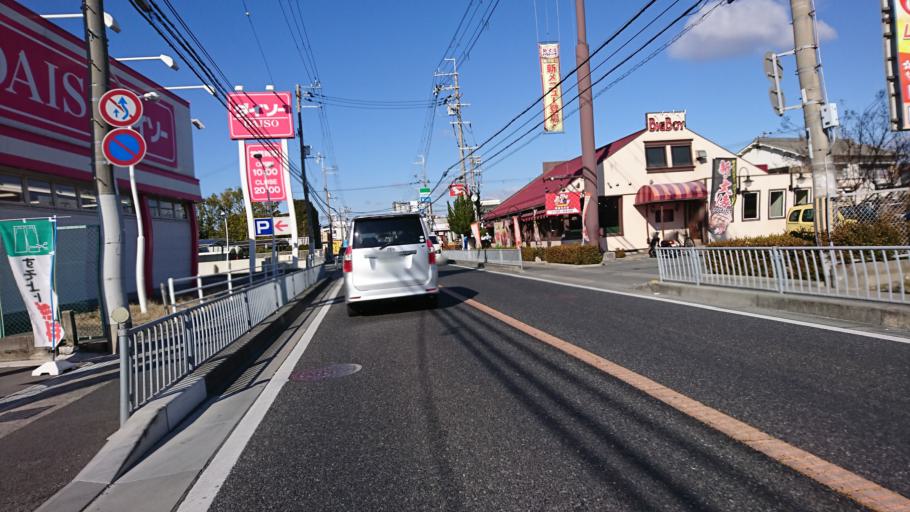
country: JP
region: Hyogo
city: Kakogawacho-honmachi
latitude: 34.7401
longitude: 134.8708
